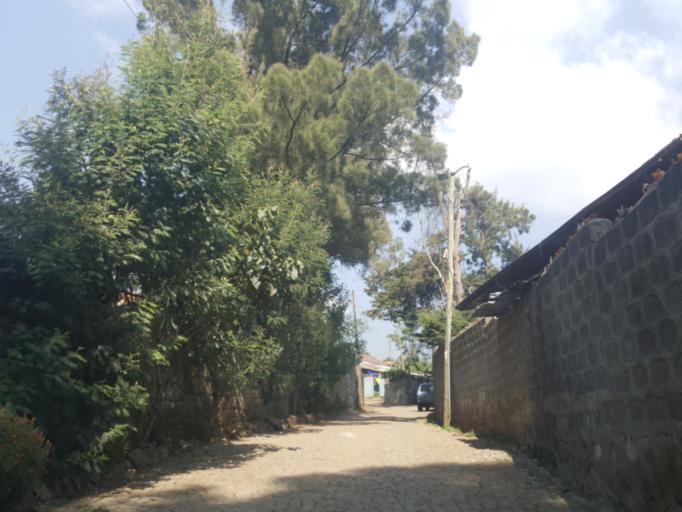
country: ET
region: Adis Abeba
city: Addis Ababa
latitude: 9.0516
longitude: 38.7353
